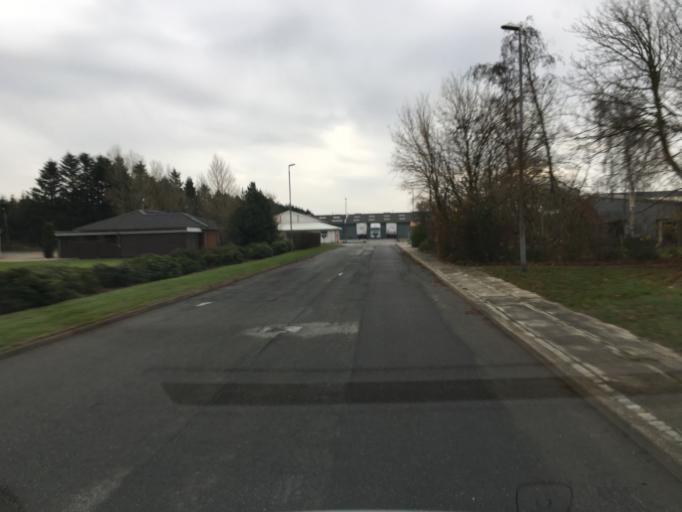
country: DK
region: South Denmark
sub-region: Tonder Kommune
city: Tonder
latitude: 54.9511
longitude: 8.8668
